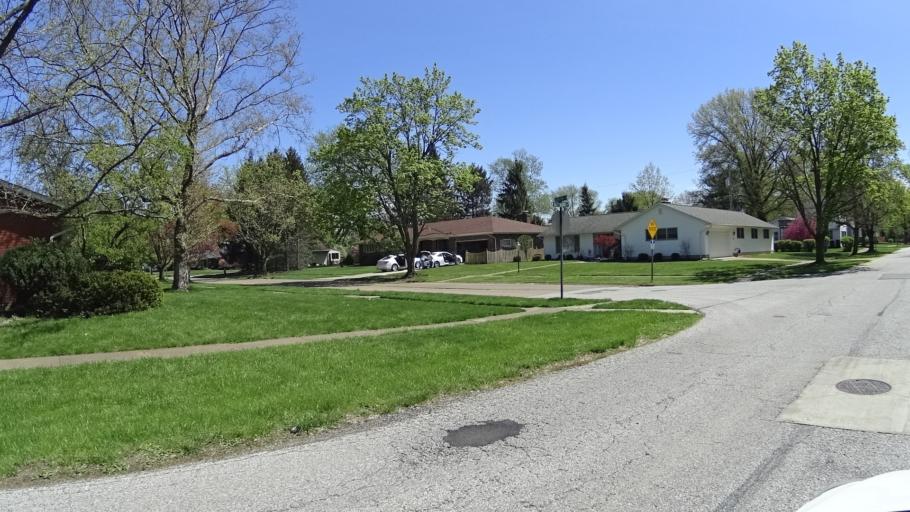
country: US
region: Ohio
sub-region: Lorain County
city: Elyria
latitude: 41.3763
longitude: -82.0999
